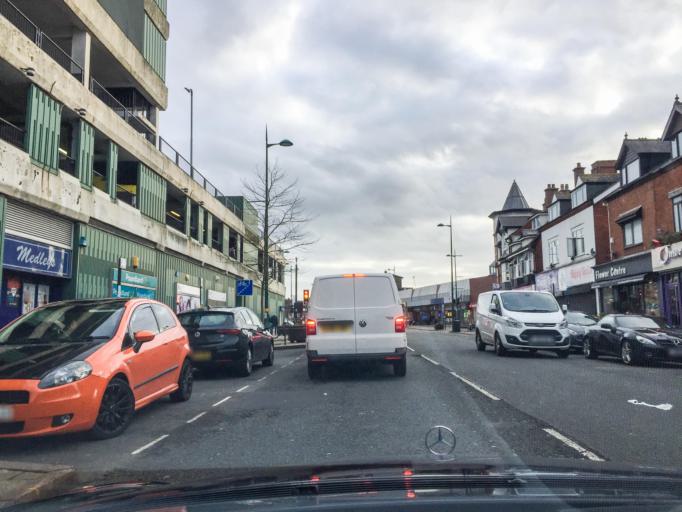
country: GB
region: England
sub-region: City and Borough of Birmingham
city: Bartley Green
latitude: 52.4170
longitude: -1.9690
